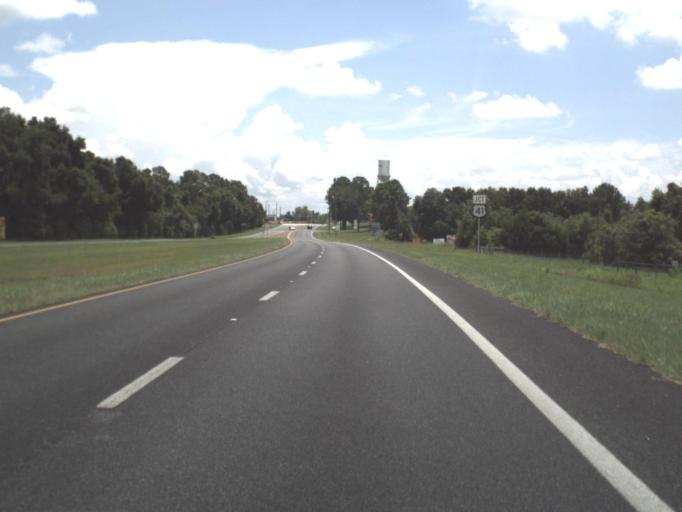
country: US
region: Florida
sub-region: Levy County
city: Williston
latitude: 29.3874
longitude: -82.4617
